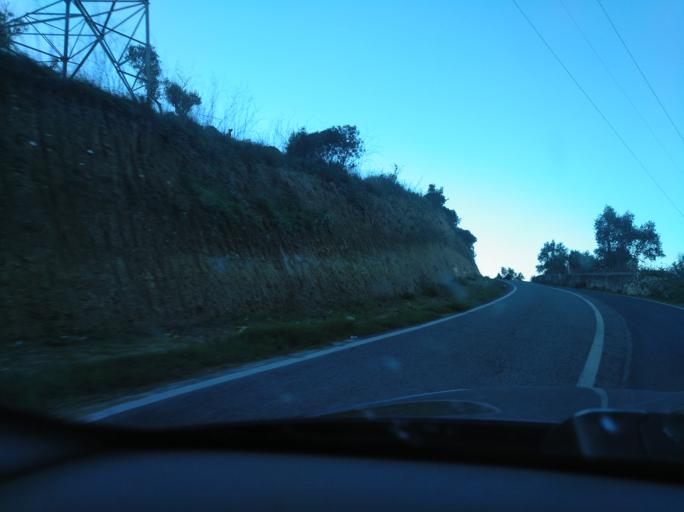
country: PT
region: Lisbon
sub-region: Loures
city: Unhos
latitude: 38.8183
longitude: -9.1149
